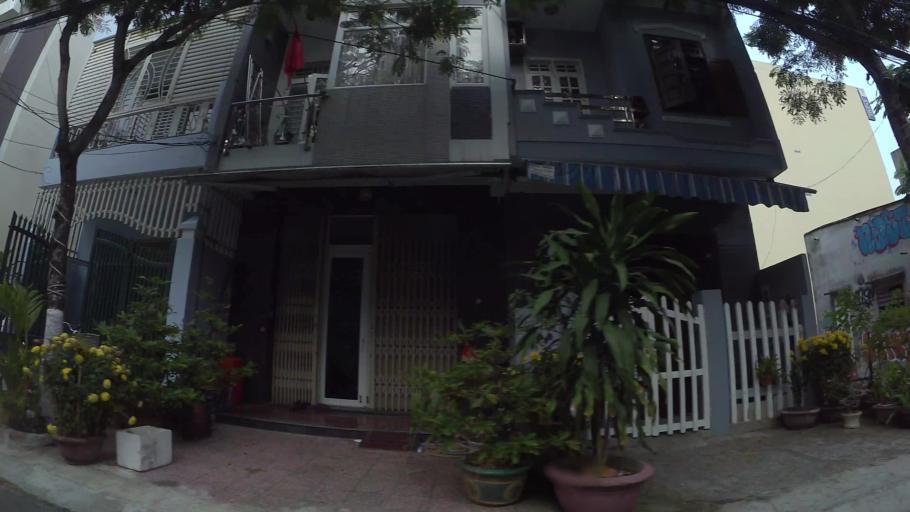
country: VN
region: Da Nang
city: Son Tra
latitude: 16.0480
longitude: 108.2454
